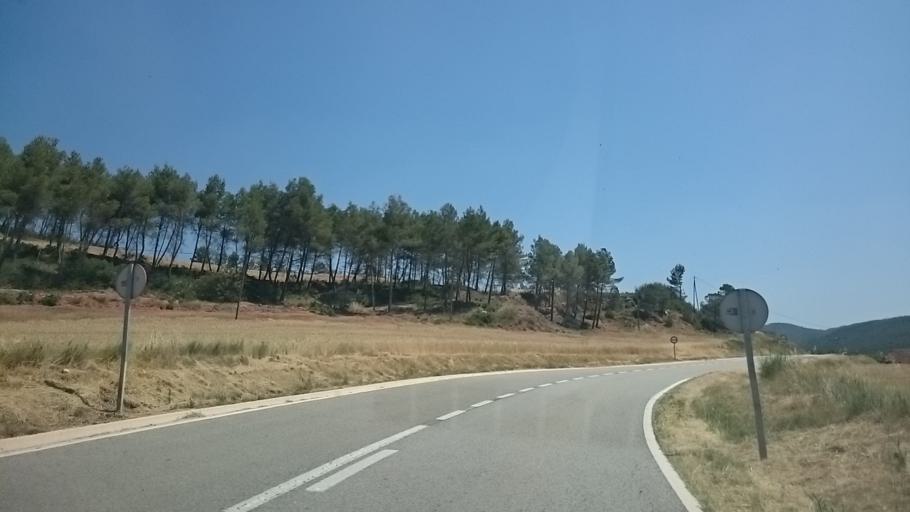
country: ES
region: Catalonia
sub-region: Provincia de Barcelona
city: Sant Marti de Tous
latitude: 41.4933
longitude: 1.5163
